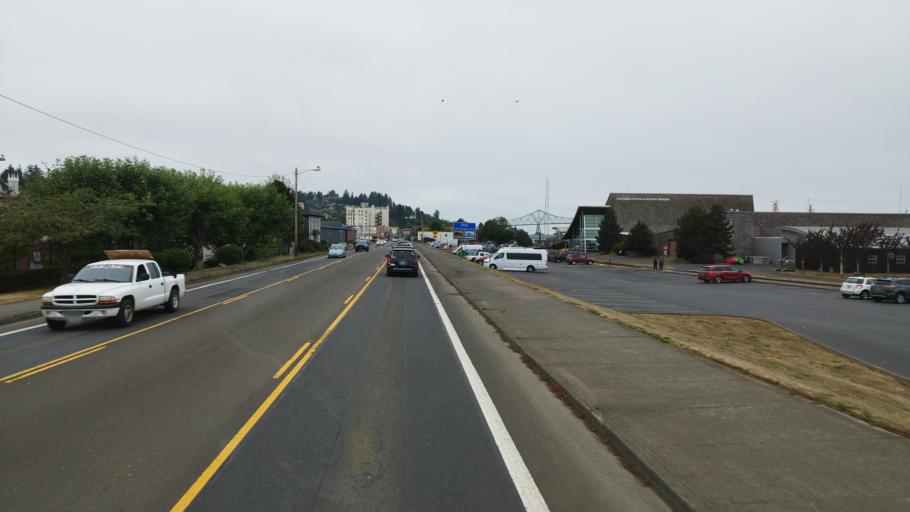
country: US
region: Oregon
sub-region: Clatsop County
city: Astoria
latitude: 46.1901
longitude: -123.8213
